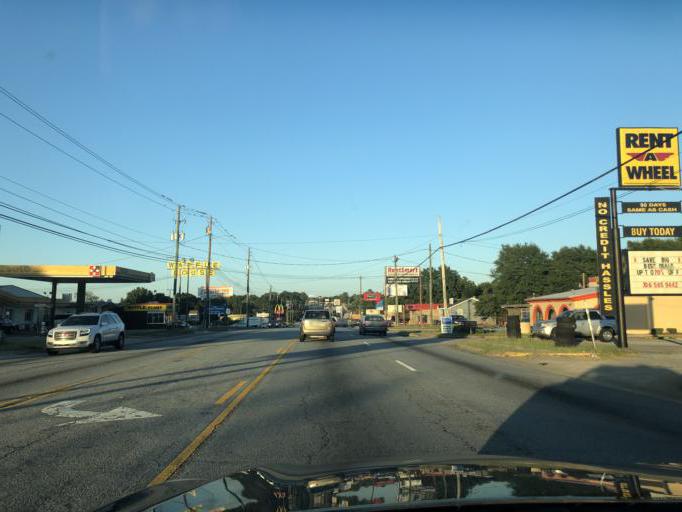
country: US
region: Georgia
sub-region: Muscogee County
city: Columbus
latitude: 32.4629
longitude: -84.9273
